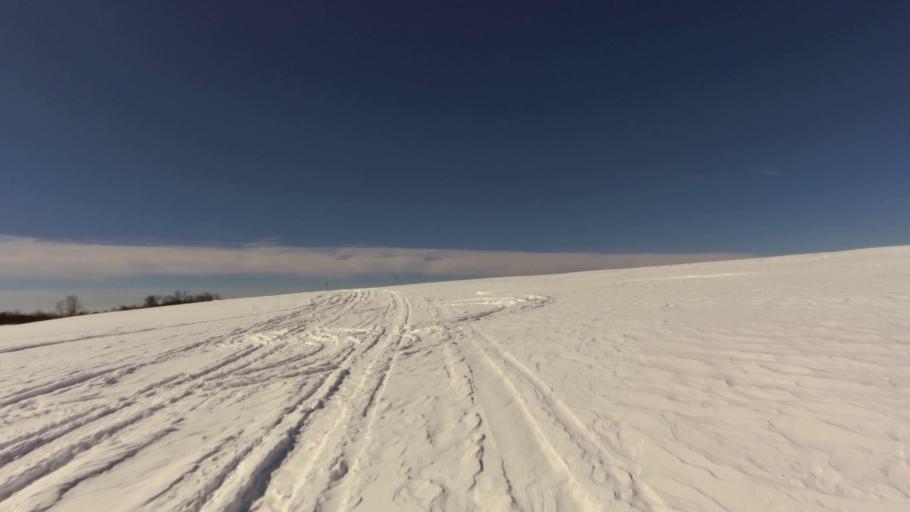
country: US
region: New York
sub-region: Allegany County
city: Cuba
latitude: 42.3117
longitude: -78.2803
